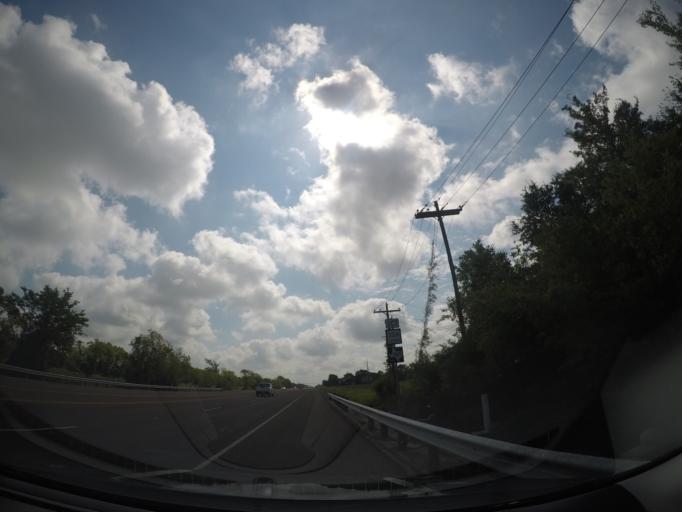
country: US
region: Texas
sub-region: Jefferson County
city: China
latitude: 30.0370
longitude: -94.4133
